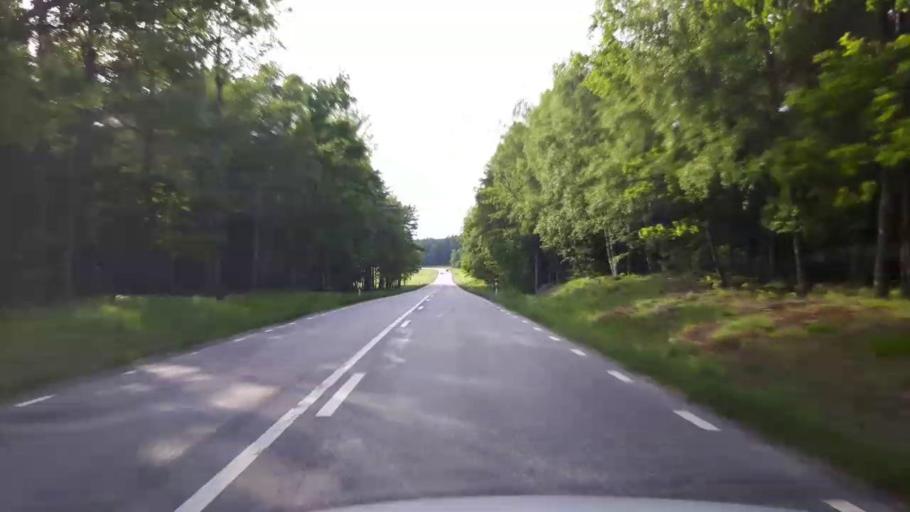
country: SE
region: Uppsala
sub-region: Habo Kommun
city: Balsta
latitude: 59.6458
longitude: 17.4311
